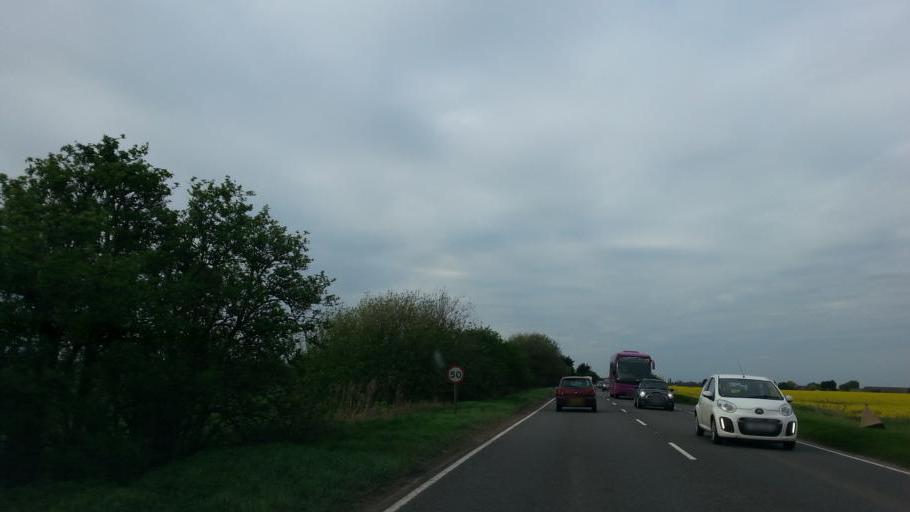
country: GB
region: England
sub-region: Cambridgeshire
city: March
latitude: 52.5811
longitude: 0.0567
